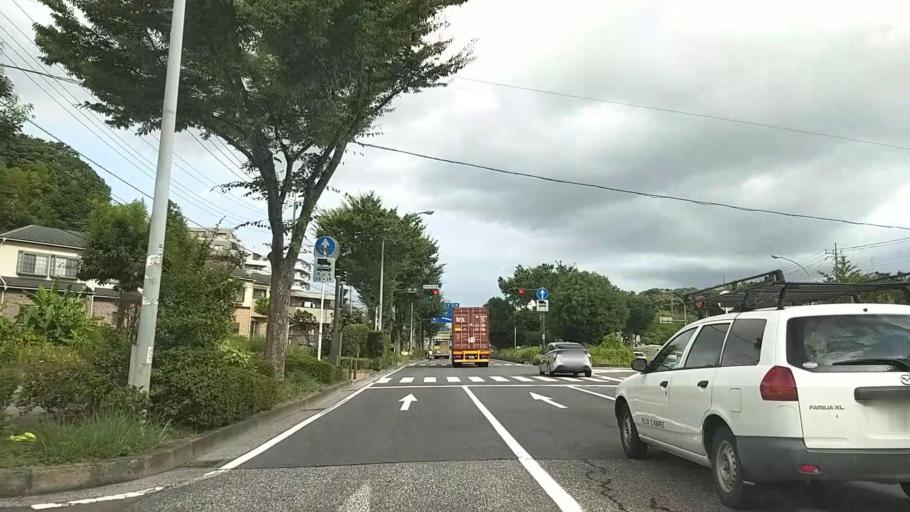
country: JP
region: Kanagawa
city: Yokohama
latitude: 35.4066
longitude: 139.5671
